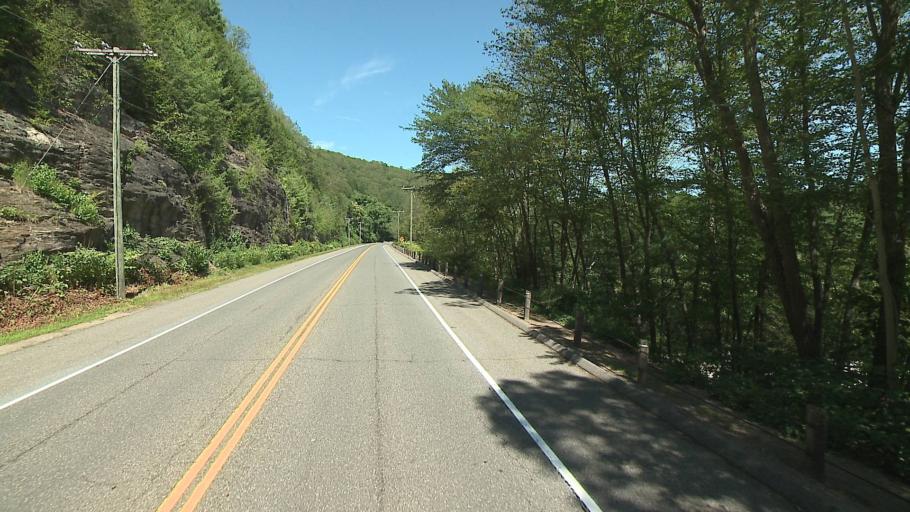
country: US
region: Connecticut
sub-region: Hartford County
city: Collinsville
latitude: 41.7998
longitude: -72.9275
